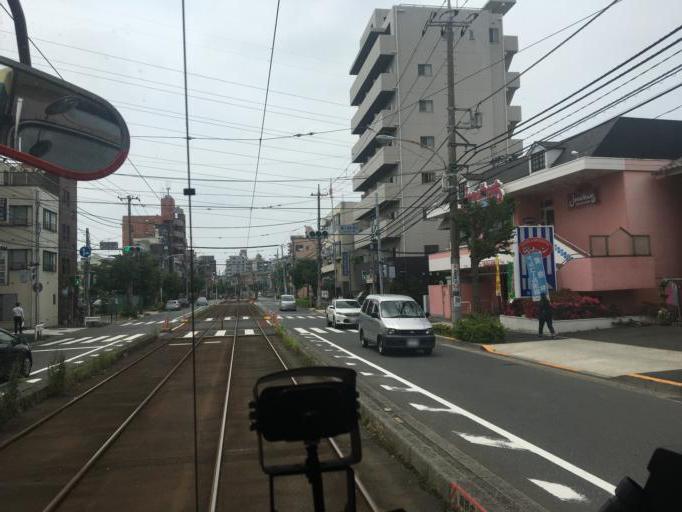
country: JP
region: Saitama
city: Kawaguchi
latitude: 35.7496
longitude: 139.7670
